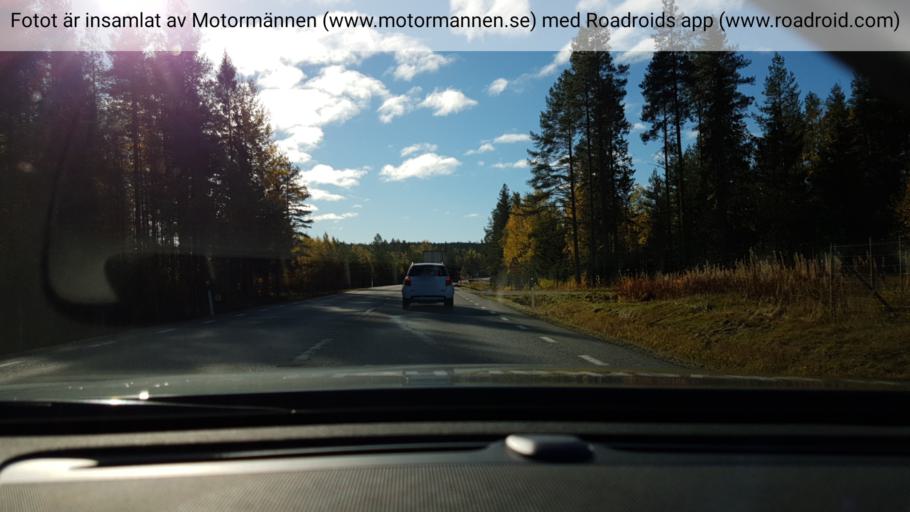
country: SE
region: Vaesterbotten
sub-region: Skelleftea Kommun
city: Burea
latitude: 64.4688
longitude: 21.2929
